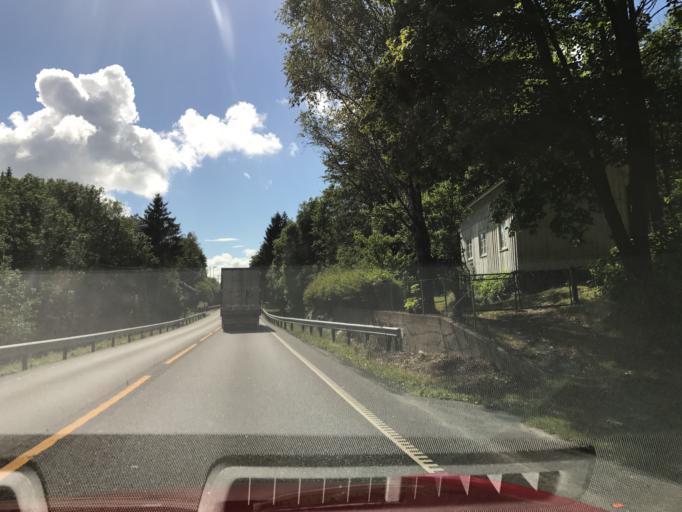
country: NO
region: Telemark
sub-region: Bamble
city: Herre
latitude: 58.9700
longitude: 9.5674
